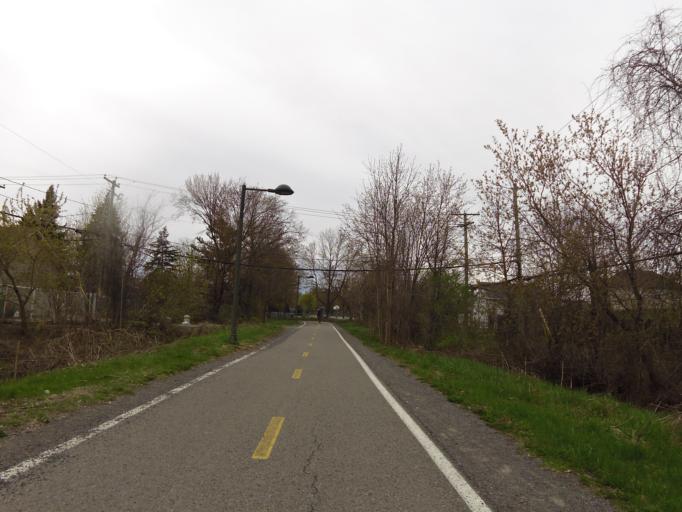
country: CA
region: Quebec
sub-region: Laurentides
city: Sainte-Marthe-sur-le-Lac
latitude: 45.5366
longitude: -73.9233
